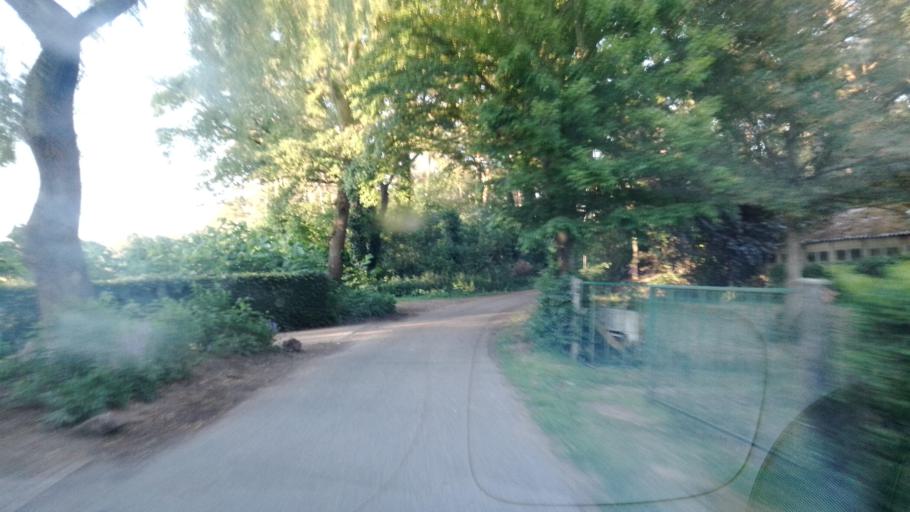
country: NL
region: Limburg
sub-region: Gemeente Peel en Maas
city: Maasbree
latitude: 51.3582
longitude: 6.0816
